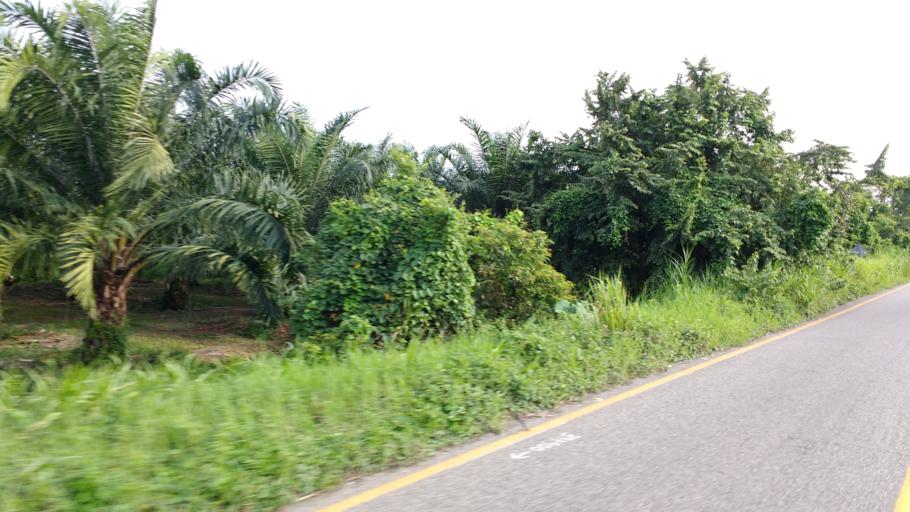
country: MX
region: Tabasco
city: Rio de Teapa
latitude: 17.6873
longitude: -92.9448
